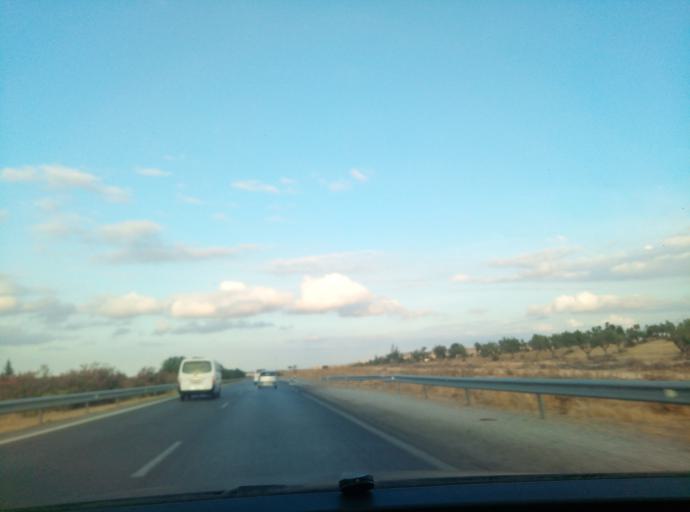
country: TN
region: Manouba
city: El Battan
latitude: 36.6661
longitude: 9.8663
